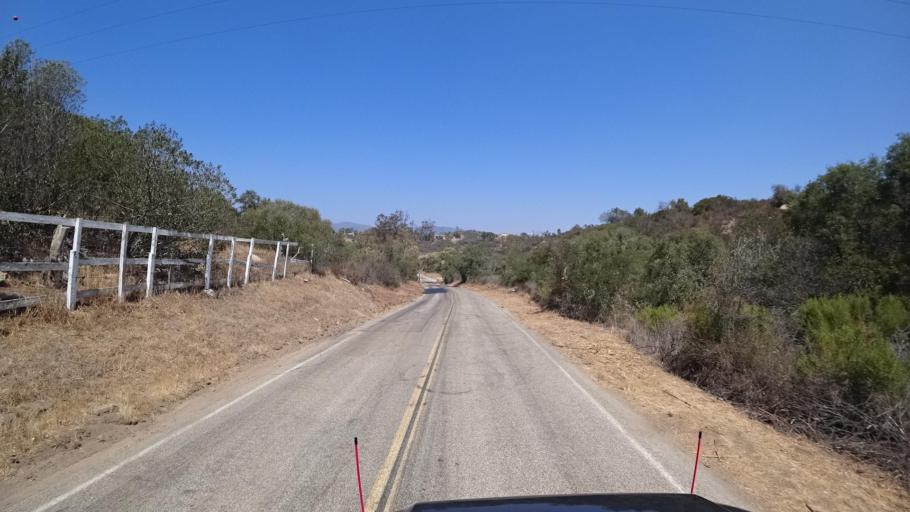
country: US
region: California
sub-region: San Diego County
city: Fallbrook
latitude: 33.4304
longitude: -117.3099
